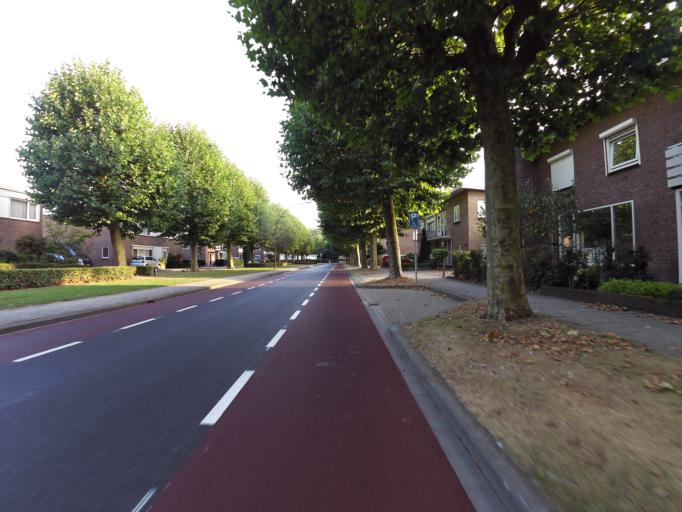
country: NL
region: Gelderland
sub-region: Gemeente Zevenaar
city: Zevenaar
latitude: 51.9254
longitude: 6.0713
